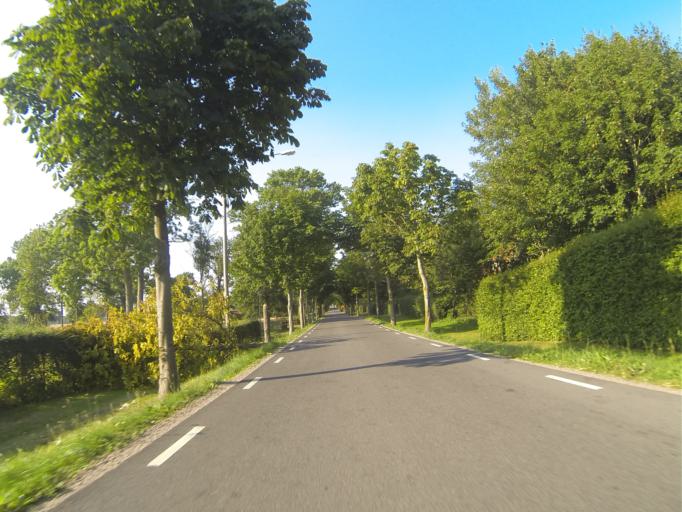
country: SE
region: Skane
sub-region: Lunds Kommun
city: Genarp
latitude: 55.6223
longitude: 13.4060
